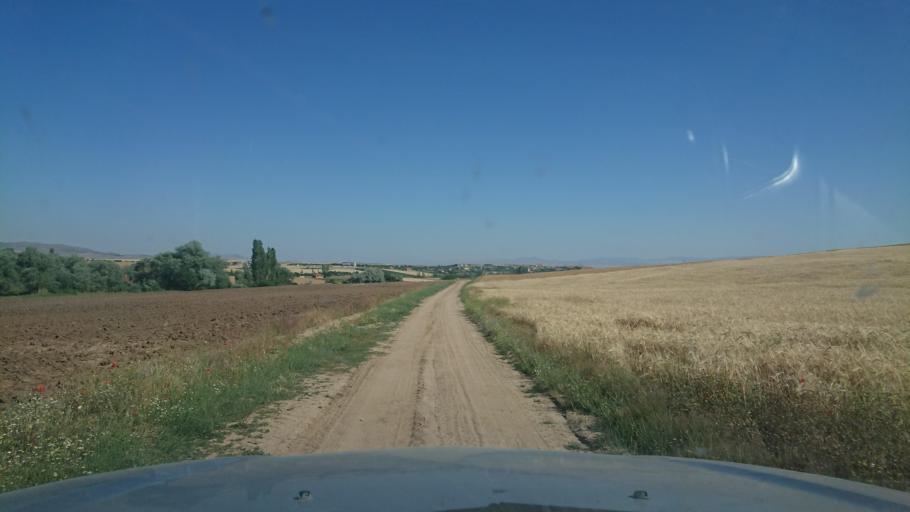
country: TR
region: Aksaray
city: Agacoren
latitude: 38.8509
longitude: 33.9153
